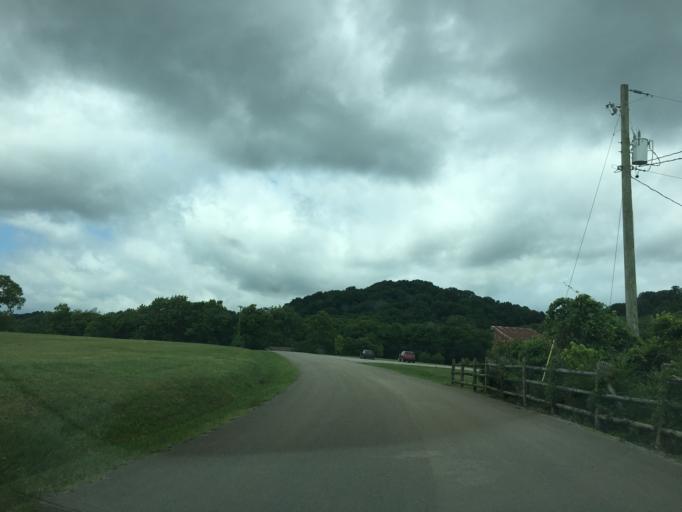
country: US
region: Tennessee
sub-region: Davidson County
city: Forest Hills
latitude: 36.0524
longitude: -86.8978
